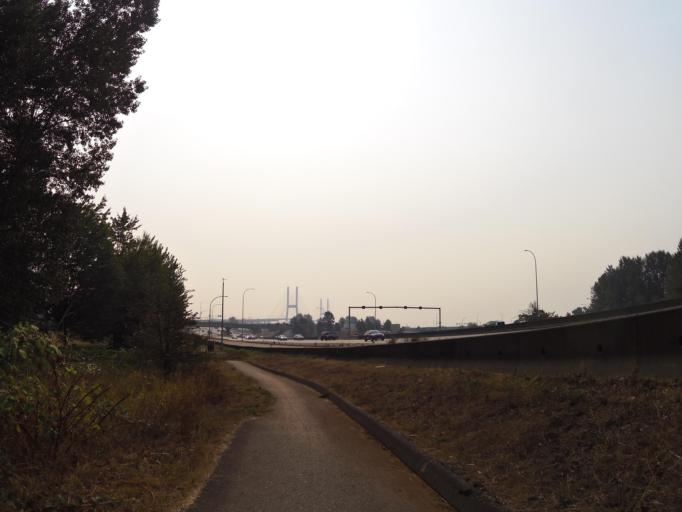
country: CA
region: British Columbia
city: New Westminster
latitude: 49.1735
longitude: -122.9537
